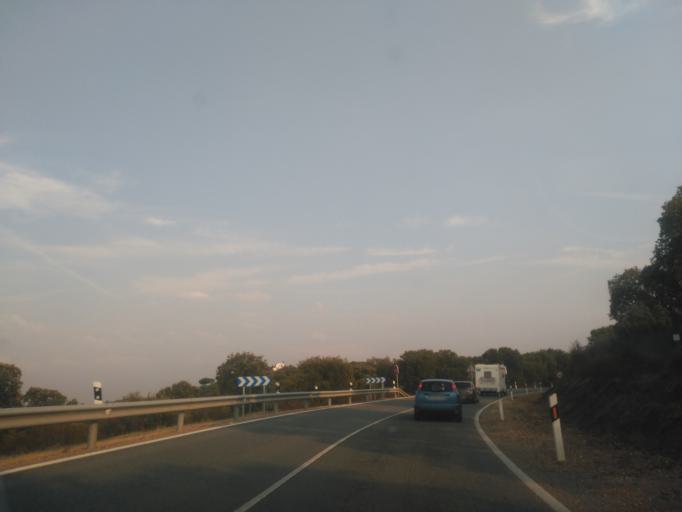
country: ES
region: Castille and Leon
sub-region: Provincia de Zamora
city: Montamarta
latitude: 41.6996
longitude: -5.8160
